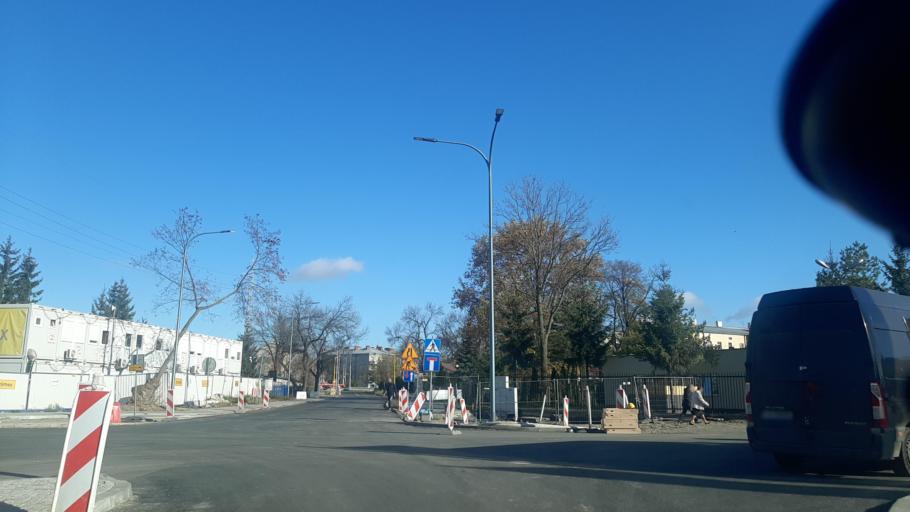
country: PL
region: Lublin Voivodeship
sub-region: Powiat lubelski
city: Lublin
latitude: 51.2328
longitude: 22.5670
